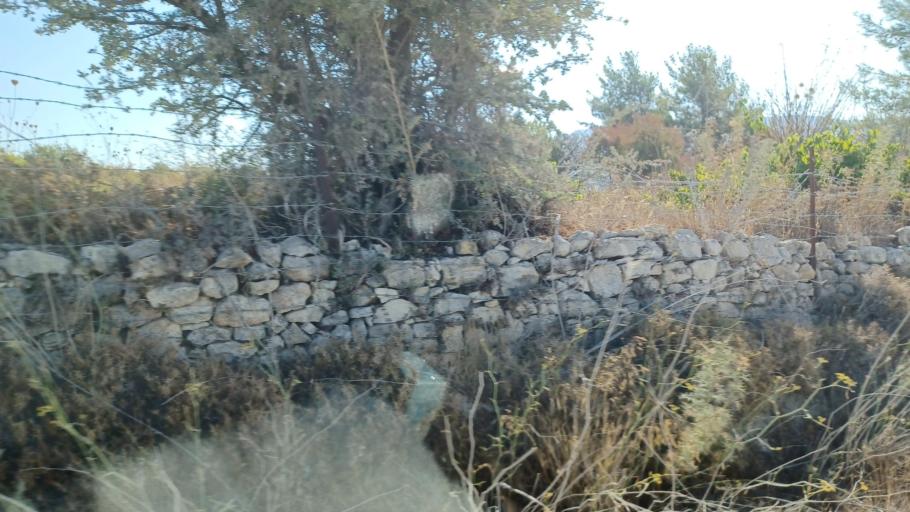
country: CY
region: Limassol
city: Pachna
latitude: 34.8427
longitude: 32.7132
